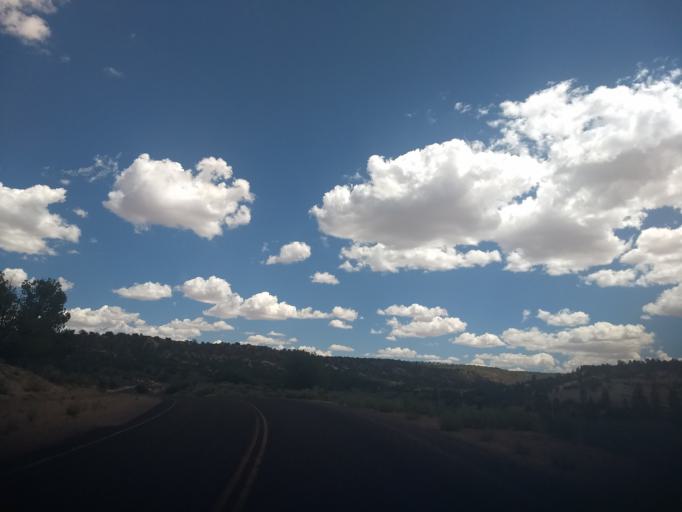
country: US
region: Utah
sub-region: Kane County
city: Kanab
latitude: 37.1238
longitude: -112.6795
